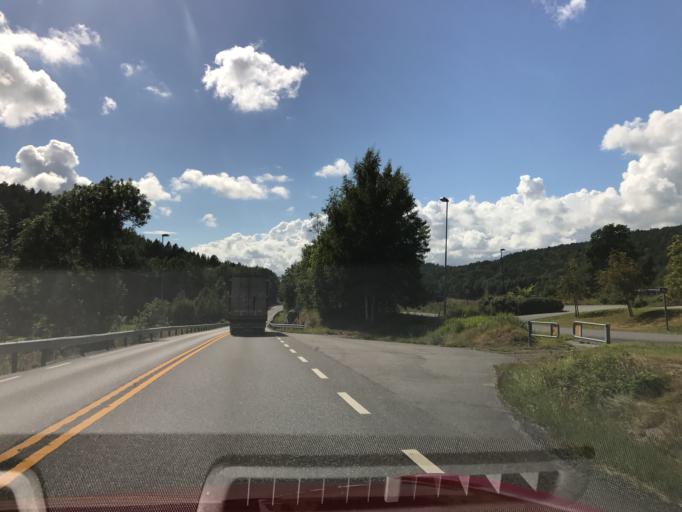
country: NO
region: Telemark
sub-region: Bamble
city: Herre
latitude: 58.9764
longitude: 9.5898
